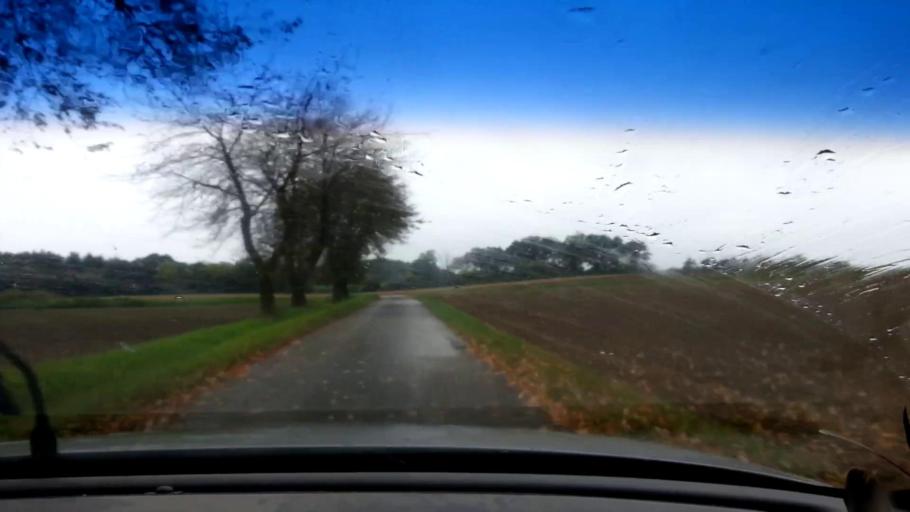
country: DE
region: Bavaria
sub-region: Upper Franconia
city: Heiligenstadt
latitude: 49.8823
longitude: 11.1538
